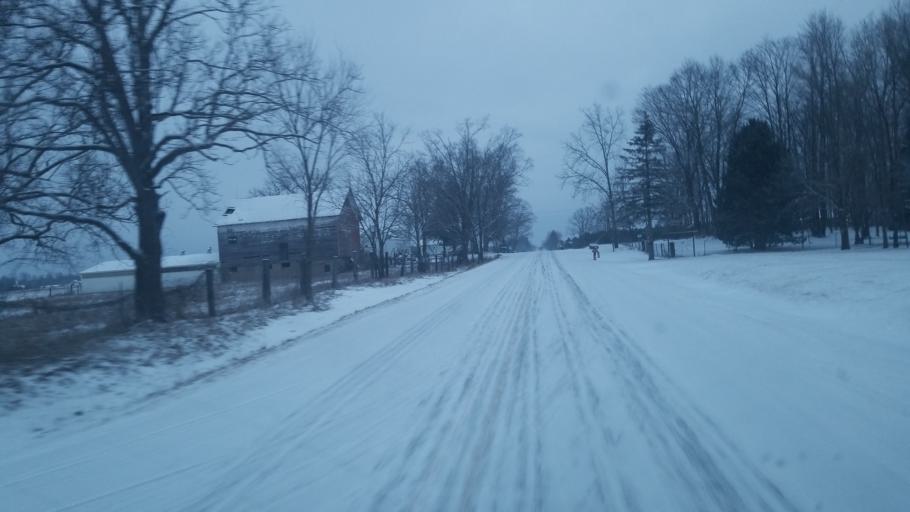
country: US
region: Michigan
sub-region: Osceola County
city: Reed City
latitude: 43.8228
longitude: -85.4241
